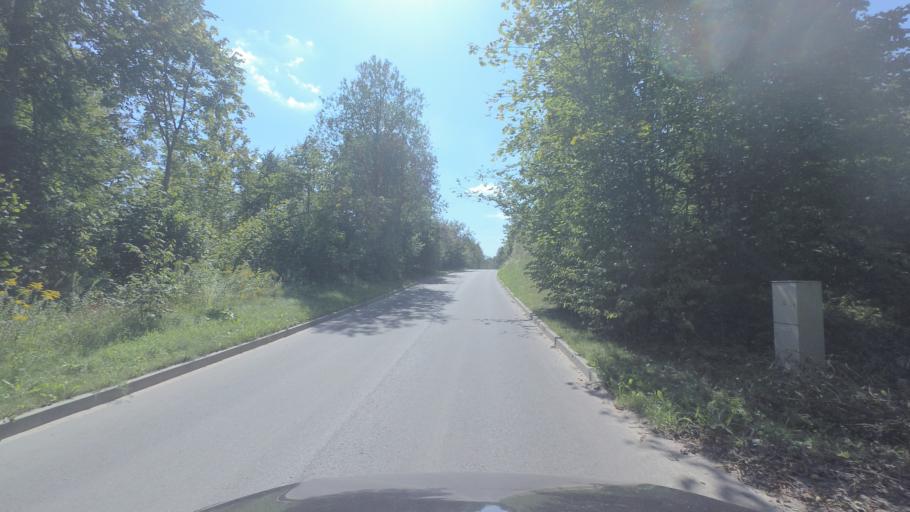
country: LT
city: Nemencine
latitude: 54.8527
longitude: 25.3757
